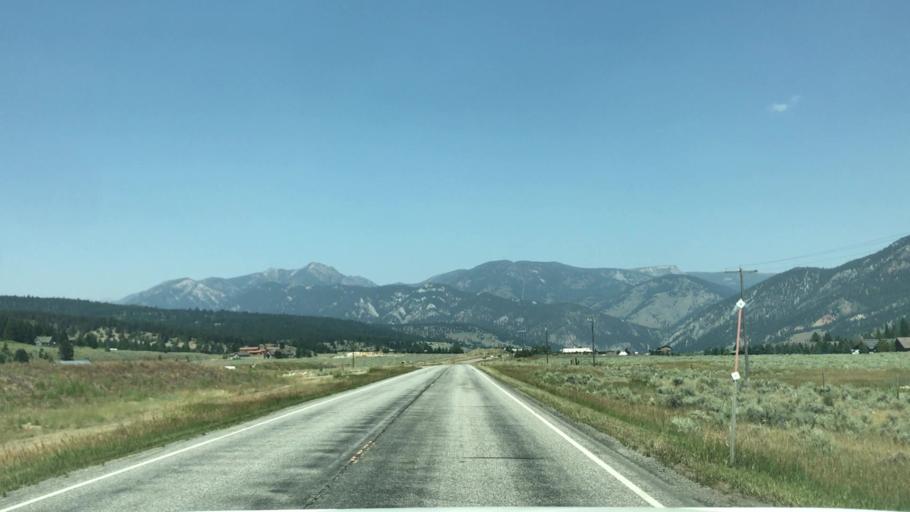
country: US
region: Montana
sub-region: Gallatin County
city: Big Sky
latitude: 45.2160
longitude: -111.2489
